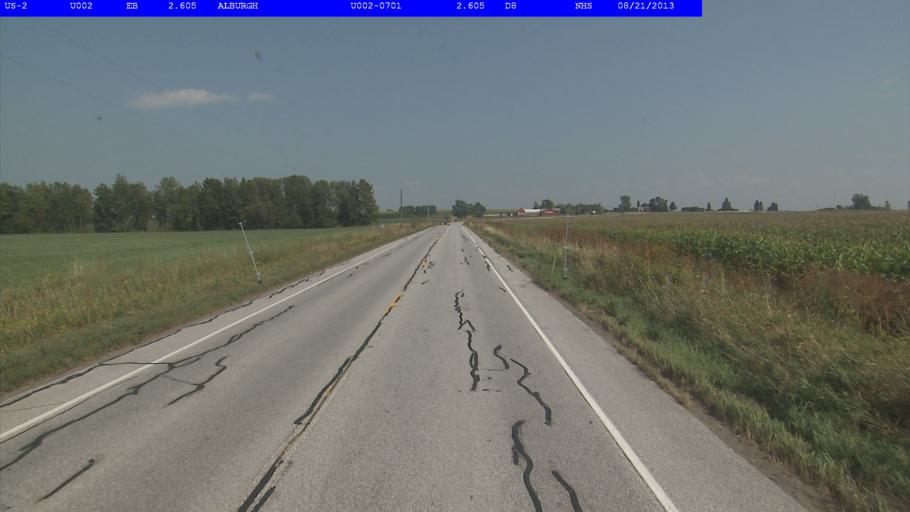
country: US
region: New York
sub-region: Clinton County
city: Rouses Point
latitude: 44.9911
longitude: -73.3054
